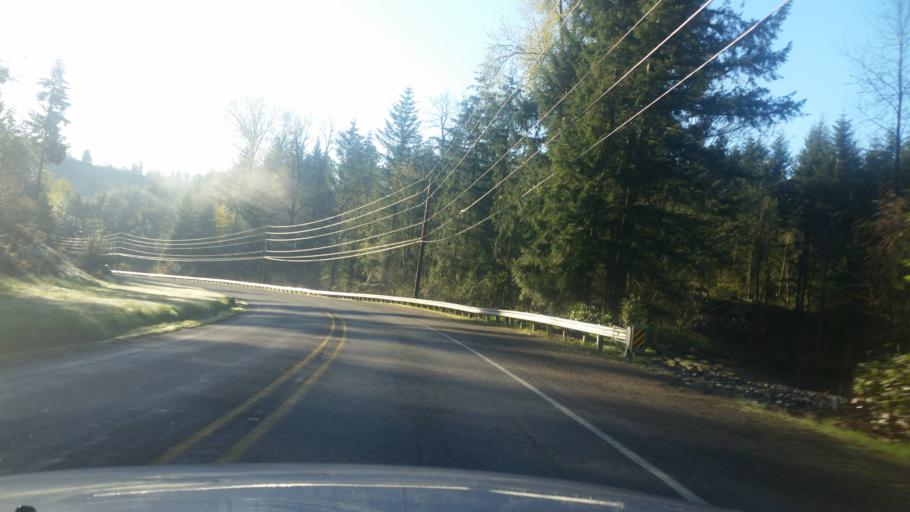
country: US
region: Washington
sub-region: Pierce County
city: Eatonville
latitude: 46.8740
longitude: -122.2979
